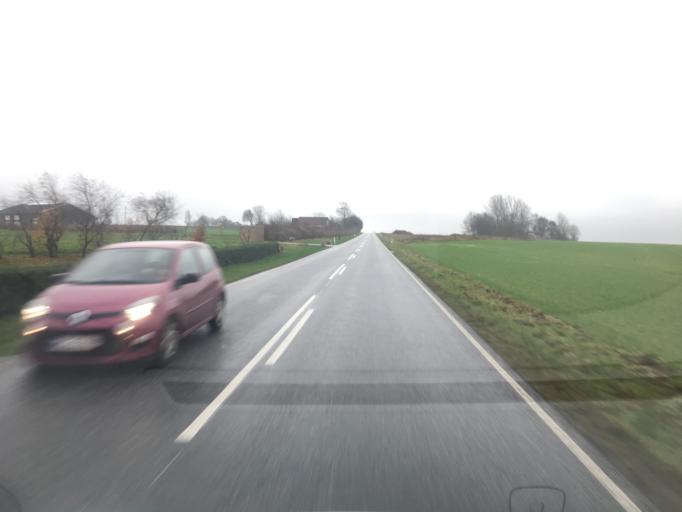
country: DK
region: Central Jutland
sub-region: Randers Kommune
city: Assentoft
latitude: 56.4185
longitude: 10.1065
